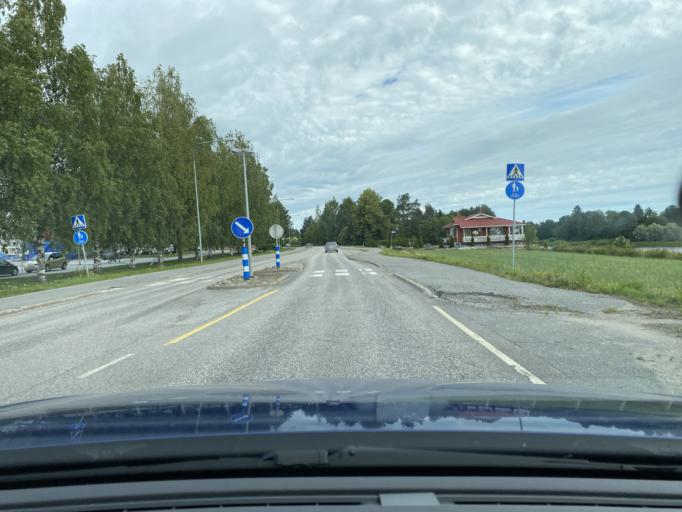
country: FI
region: Ostrobothnia
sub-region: Vaasa
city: Vaehaekyroe
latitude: 63.0475
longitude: 22.1161
